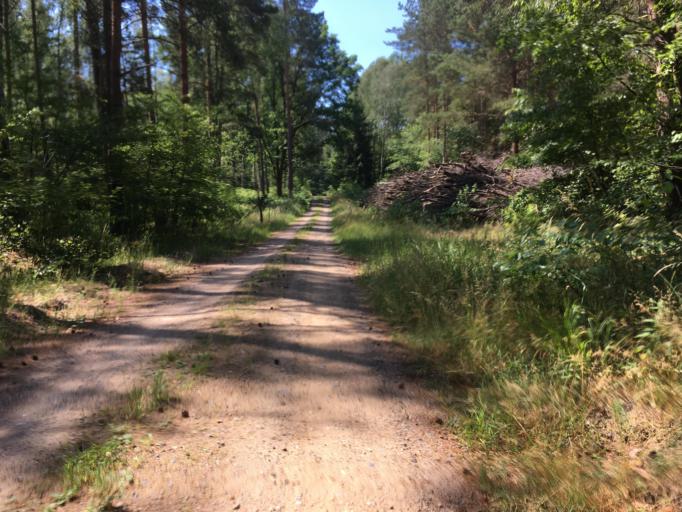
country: DE
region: Brandenburg
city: Marienwerder
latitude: 52.9231
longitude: 13.6489
